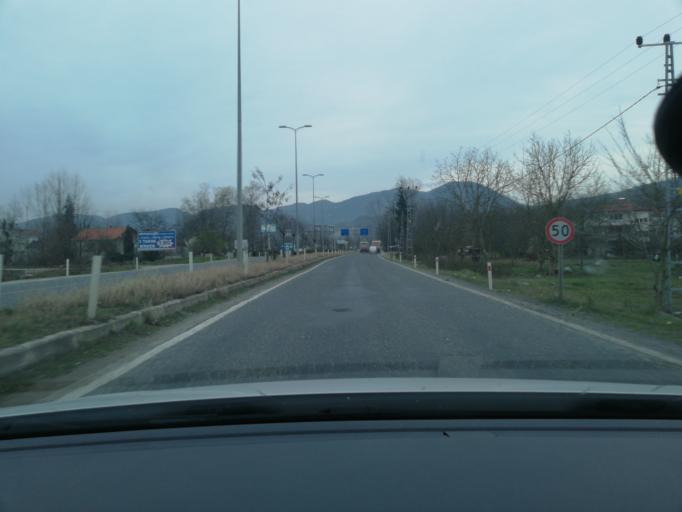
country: TR
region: Zonguldak
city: Gokcebey
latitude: 41.3006
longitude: 32.1178
